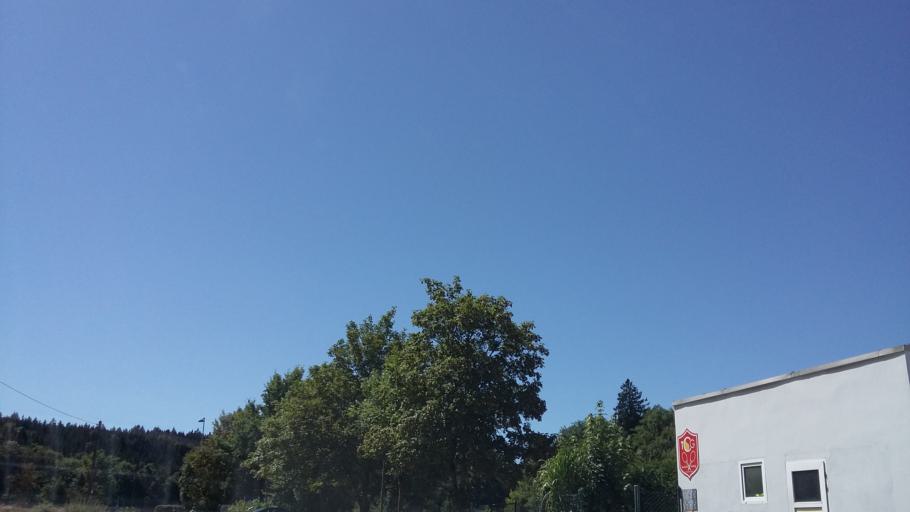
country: DE
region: Bavaria
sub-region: Upper Bavaria
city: Gauting
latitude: 48.0594
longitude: 11.3800
